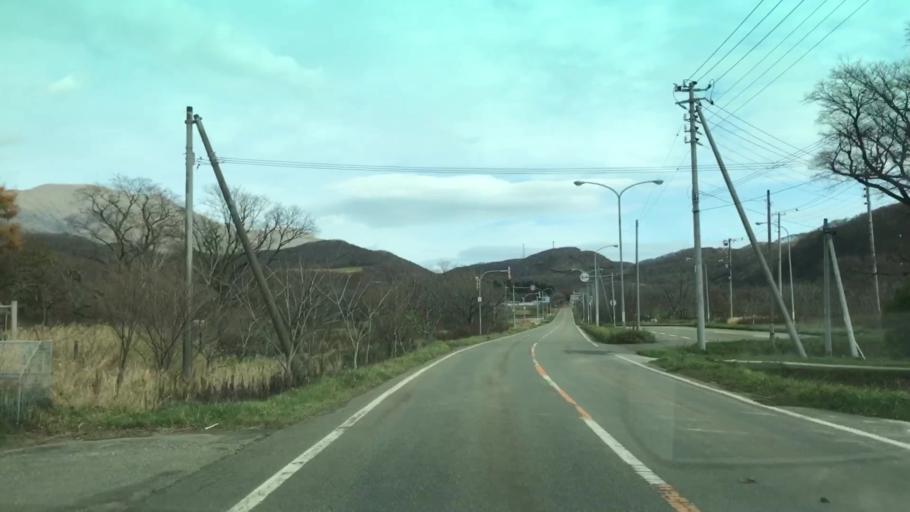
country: JP
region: Hokkaido
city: Shizunai-furukawacho
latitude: 42.0235
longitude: 143.2043
